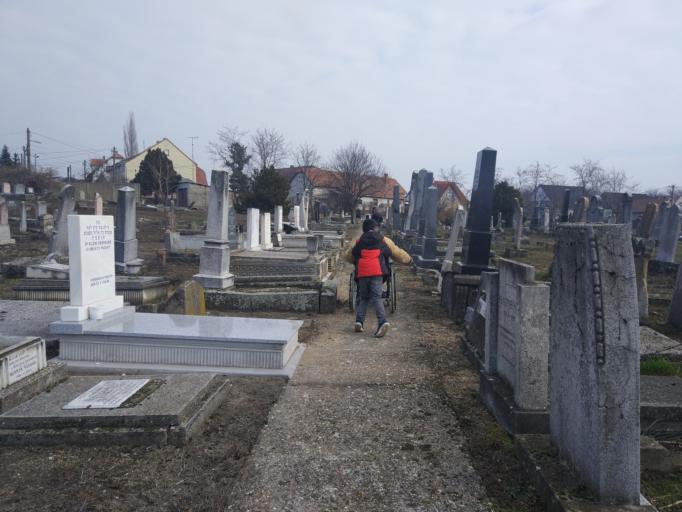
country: HU
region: Hajdu-Bihar
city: Debrecen
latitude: 47.5129
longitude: 21.6397
